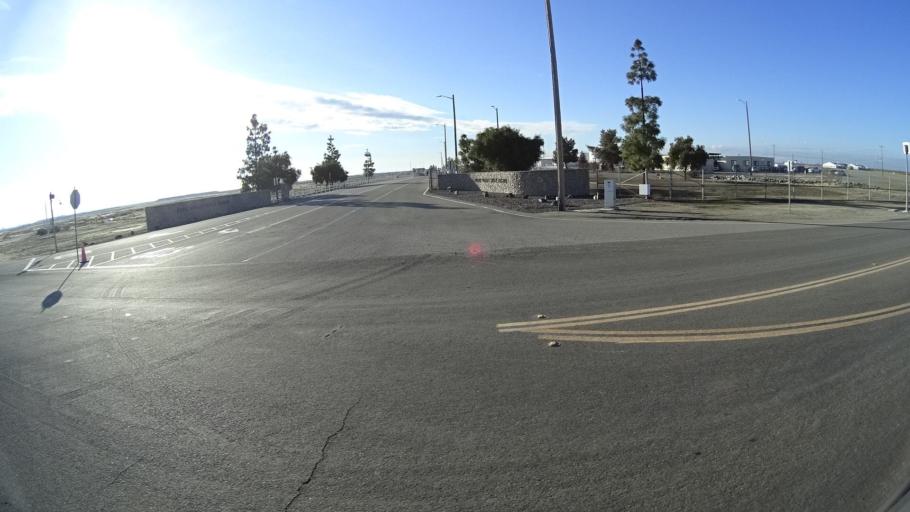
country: US
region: California
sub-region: Kern County
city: Delano
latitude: 35.7759
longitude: -119.3213
